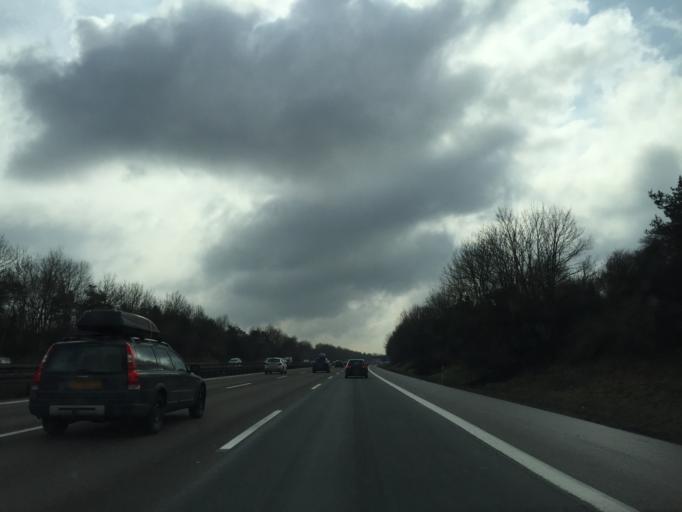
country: DE
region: Bavaria
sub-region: Upper Bavaria
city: Manching
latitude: 48.7219
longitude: 11.4787
